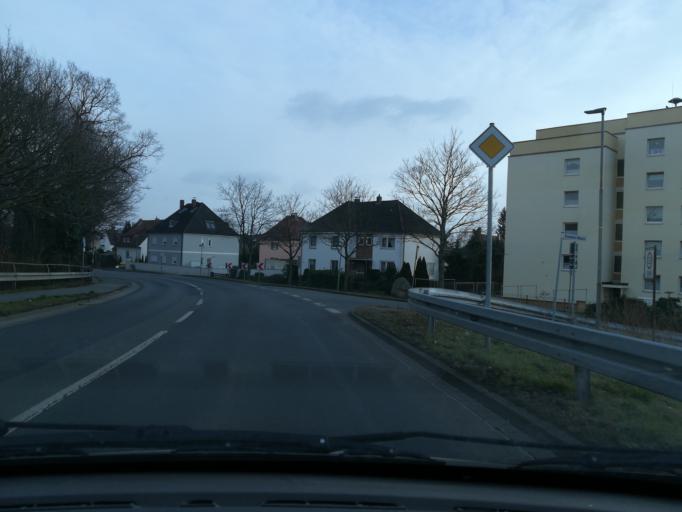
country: DE
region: Lower Saxony
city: Garbsen
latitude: 52.3979
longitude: 9.5708
